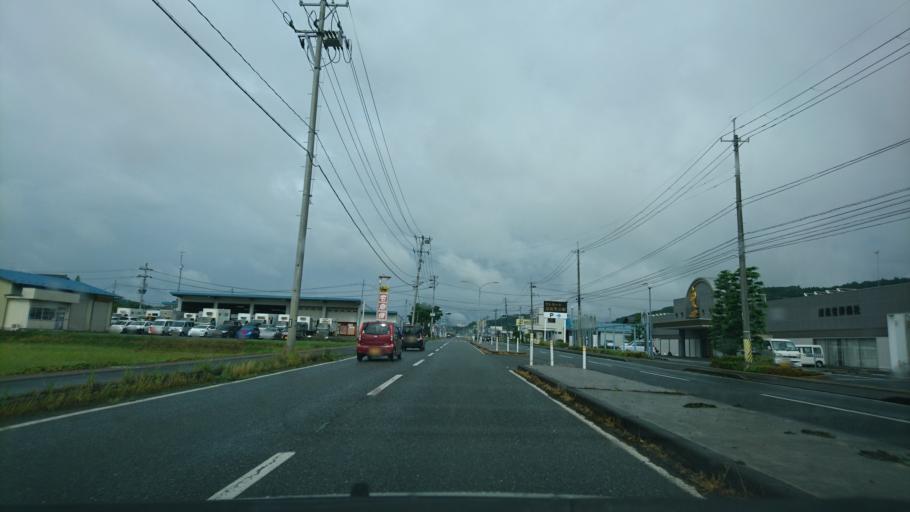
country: JP
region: Iwate
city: Ichinoseki
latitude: 38.9396
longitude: 141.0967
